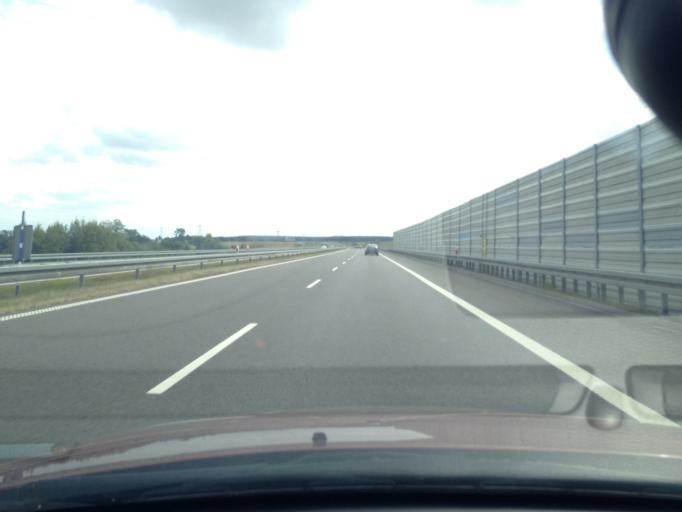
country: PL
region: West Pomeranian Voivodeship
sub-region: Powiat pyrzycki
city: Bielice
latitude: 53.2443
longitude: 14.6364
